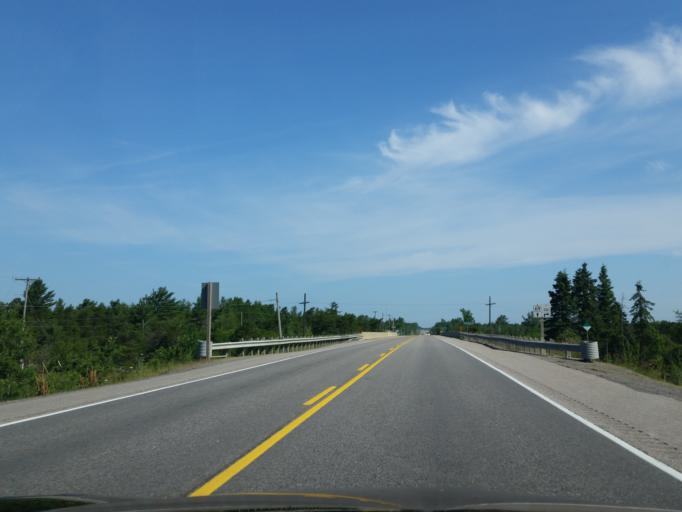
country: CA
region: Ontario
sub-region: Parry Sound District
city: Parry Sound
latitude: 45.7991
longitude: -80.5354
